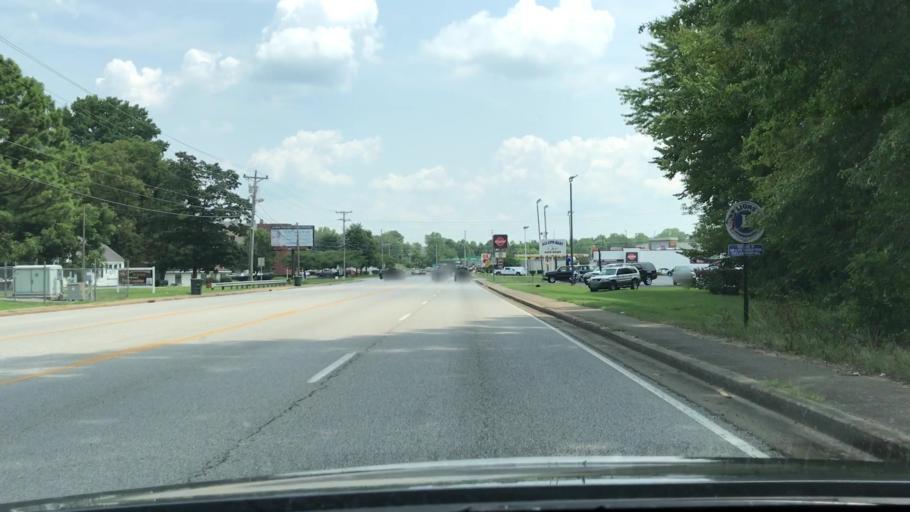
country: US
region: Tennessee
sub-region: Sumner County
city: Portland
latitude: 36.5768
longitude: -86.5184
